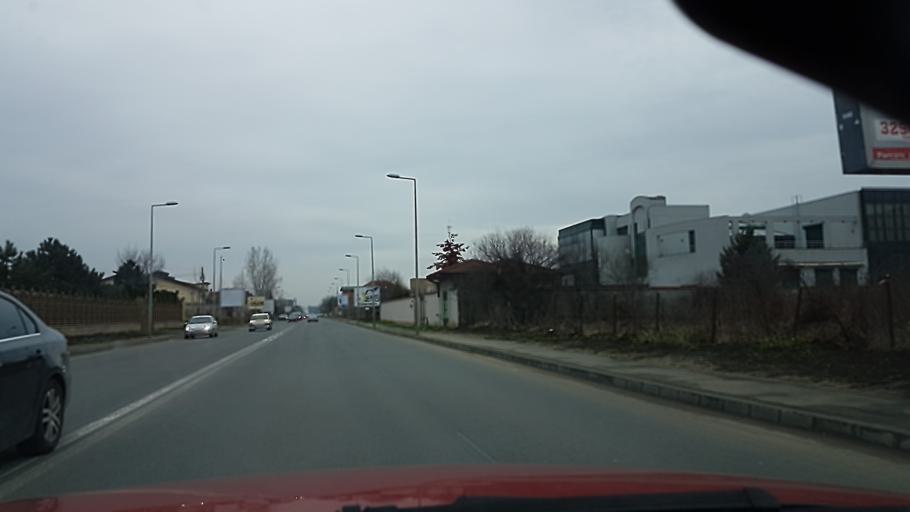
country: RO
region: Ilfov
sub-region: Comuna Tunari
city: Tunari
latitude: 44.5176
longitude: 26.1420
